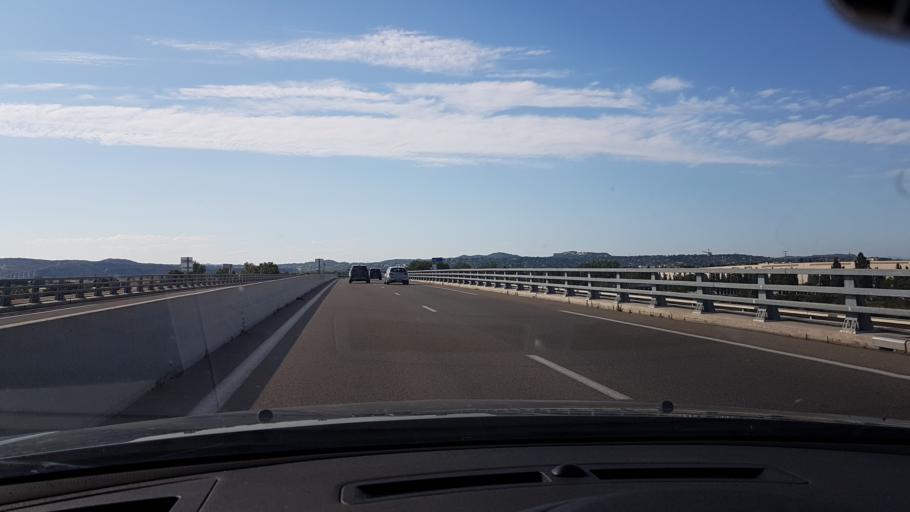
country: FR
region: Provence-Alpes-Cote d'Azur
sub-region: Departement des Bouches-du-Rhone
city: Rognonas
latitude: 43.9172
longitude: 4.7844
